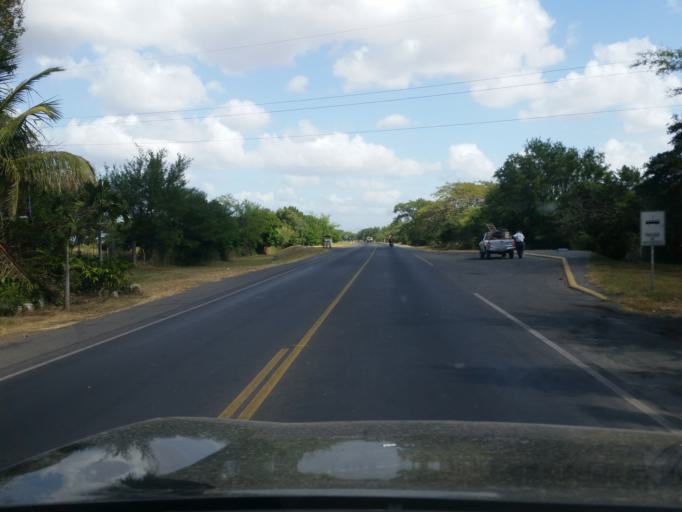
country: NI
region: Managua
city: Tipitapa
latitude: 12.1774
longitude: -86.1124
